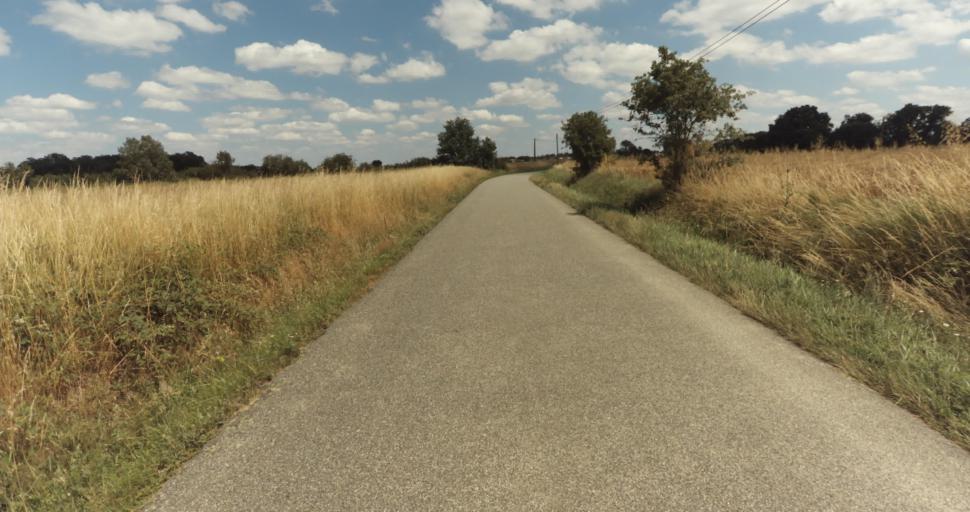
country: FR
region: Midi-Pyrenees
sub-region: Departement de la Haute-Garonne
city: Fontenilles
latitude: 43.5623
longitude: 1.1784
